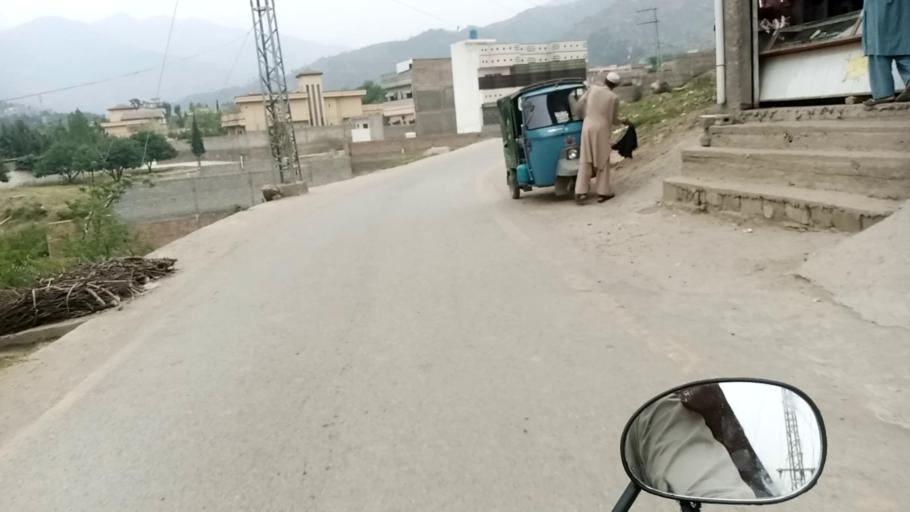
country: PK
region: Khyber Pakhtunkhwa
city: Mingora
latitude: 34.7593
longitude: 72.3768
